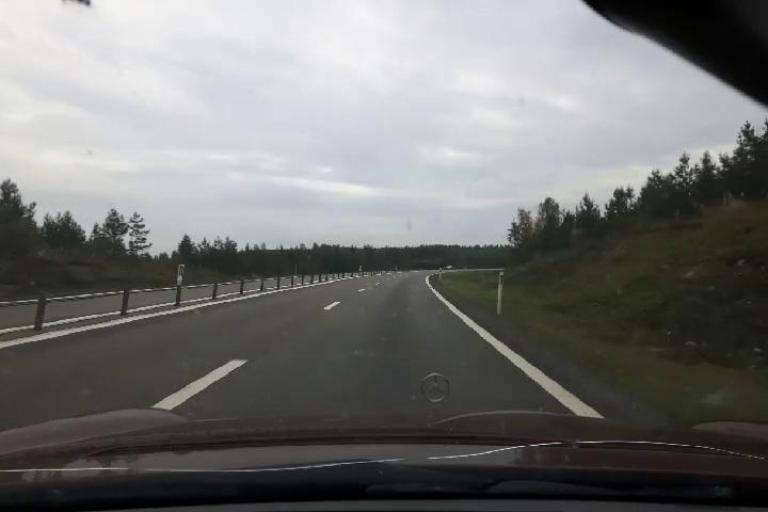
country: SE
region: Vaesternorrland
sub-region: Haernoesands Kommun
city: Haernoesand
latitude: 62.7261
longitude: 17.9227
